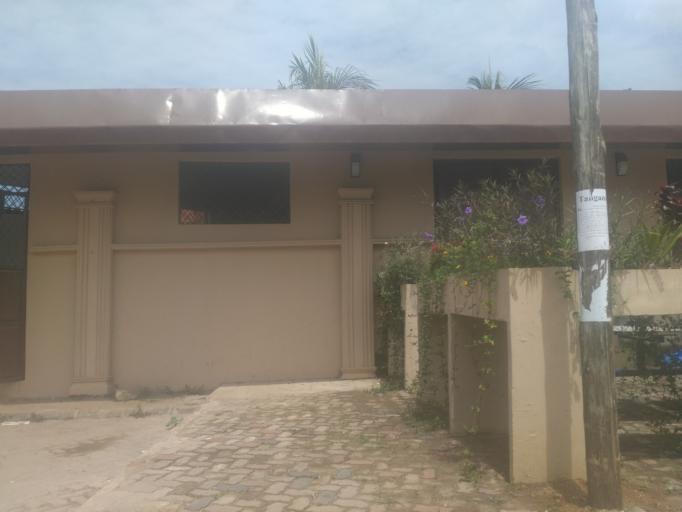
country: TZ
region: Zanzibar Urban/West
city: Zanzibar
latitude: -6.2290
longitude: 39.2143
